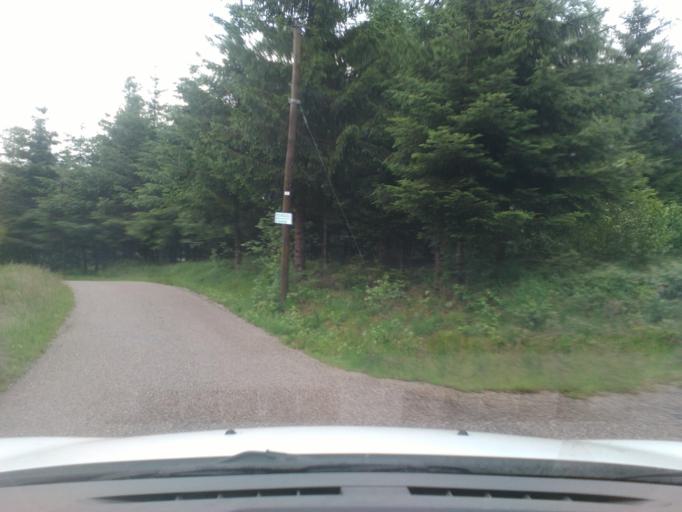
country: FR
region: Lorraine
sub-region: Departement des Vosges
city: Le Tholy
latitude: 48.1171
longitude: 6.7068
